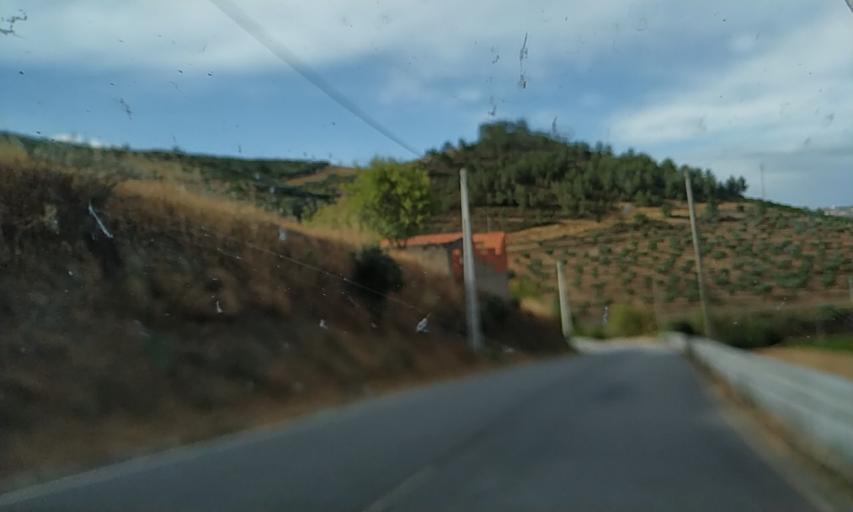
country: PT
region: Viseu
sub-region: Sao Joao da Pesqueira
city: Sao Joao da Pesqueira
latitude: 41.0943
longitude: -7.4681
